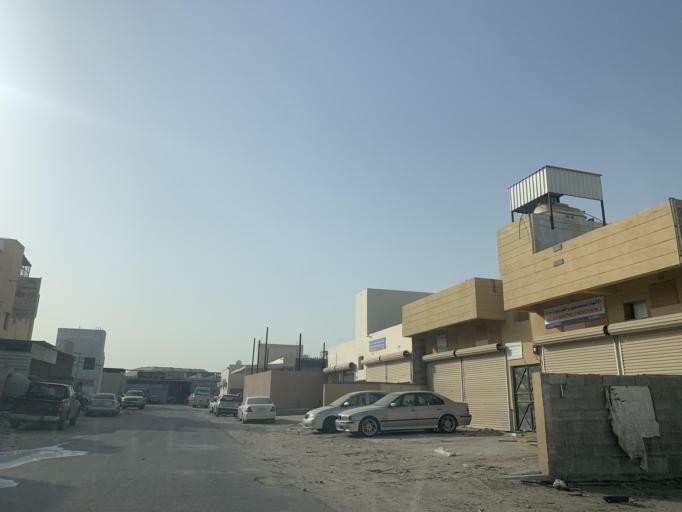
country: BH
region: Central Governorate
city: Madinat Hamad
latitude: 26.1460
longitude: 50.4846
